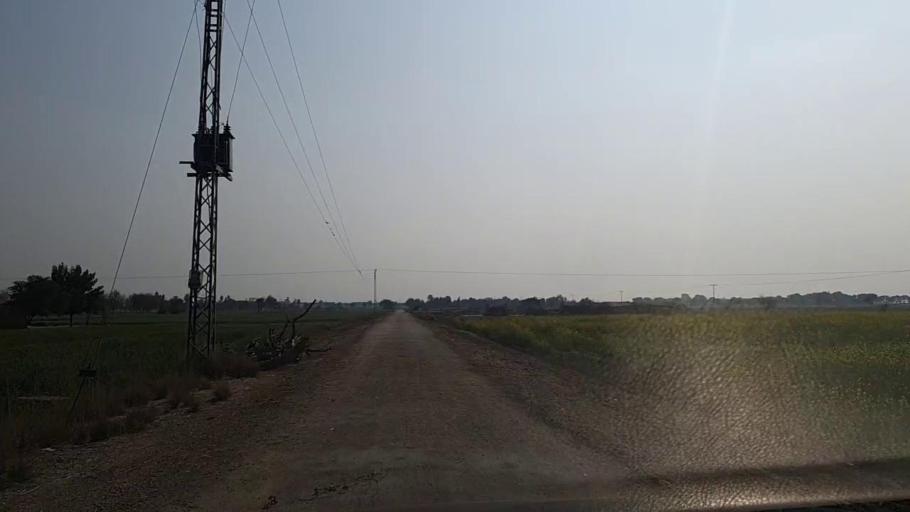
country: PK
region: Sindh
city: Daur
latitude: 26.4049
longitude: 68.4201
